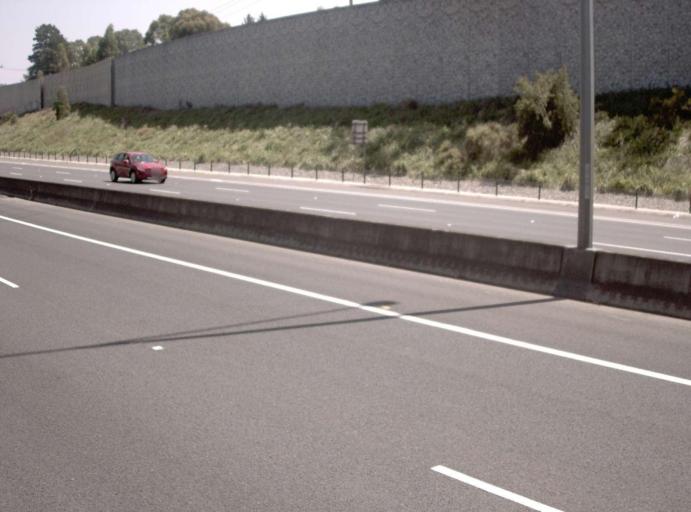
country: AU
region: Victoria
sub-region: Whitehorse
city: Mont Albert North
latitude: -37.7937
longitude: 145.1090
